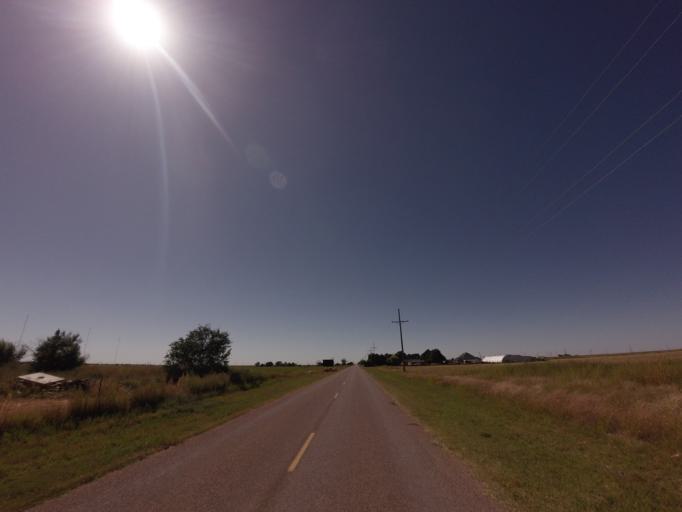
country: US
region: New Mexico
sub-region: Curry County
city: Clovis
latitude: 34.4483
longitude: -103.2008
